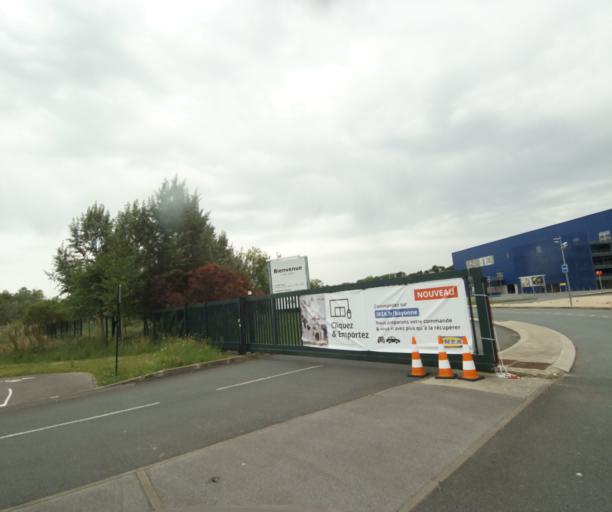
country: FR
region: Aquitaine
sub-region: Departement des Pyrenees-Atlantiques
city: Mouguerre
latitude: 43.4801
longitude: -1.4425
